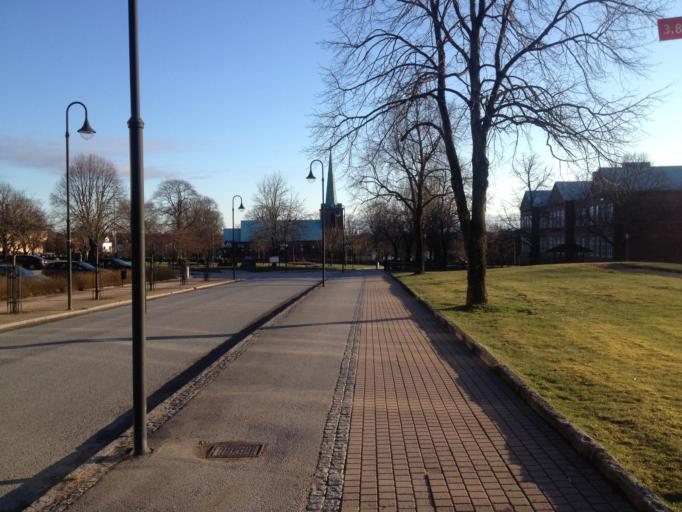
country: SE
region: Joenkoeping
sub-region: Gislaveds Kommun
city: Gislaved
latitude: 57.3036
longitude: 13.5385
